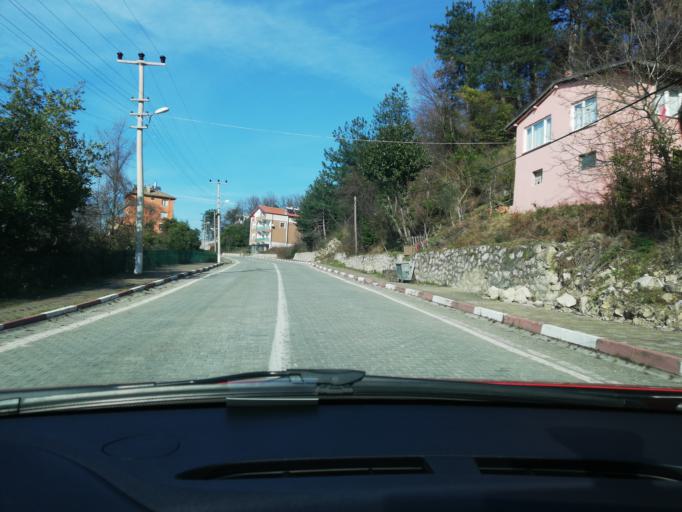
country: TR
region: Bartin
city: Kurucasile
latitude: 41.8436
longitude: 32.7304
